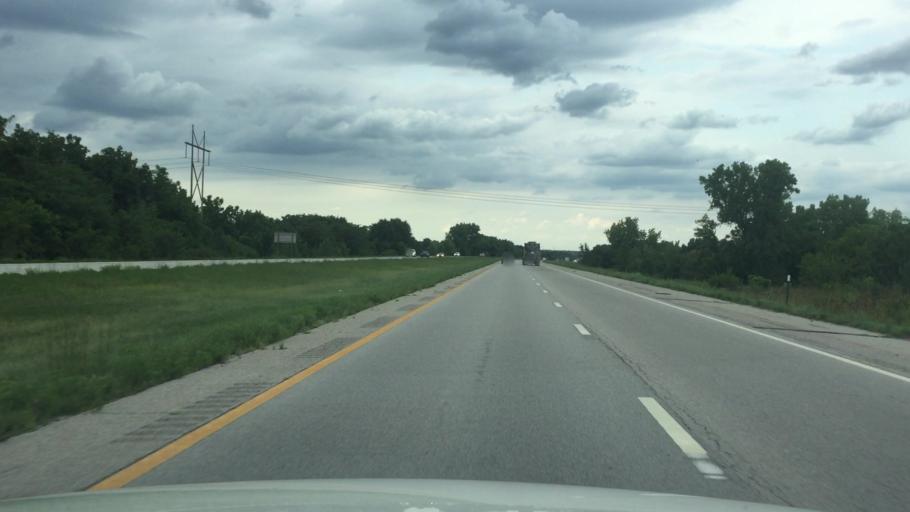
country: US
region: Missouri
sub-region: Cass County
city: Belton
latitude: 38.7768
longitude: -94.6777
